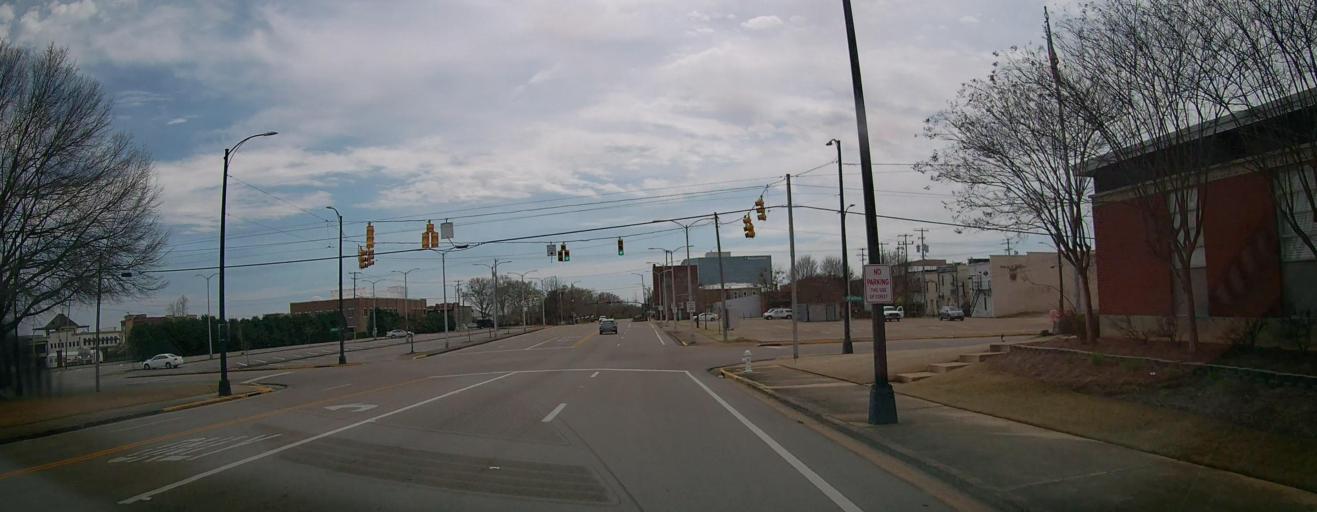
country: US
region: Mississippi
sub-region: Lee County
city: Tupelo
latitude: 34.2596
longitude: -88.7035
